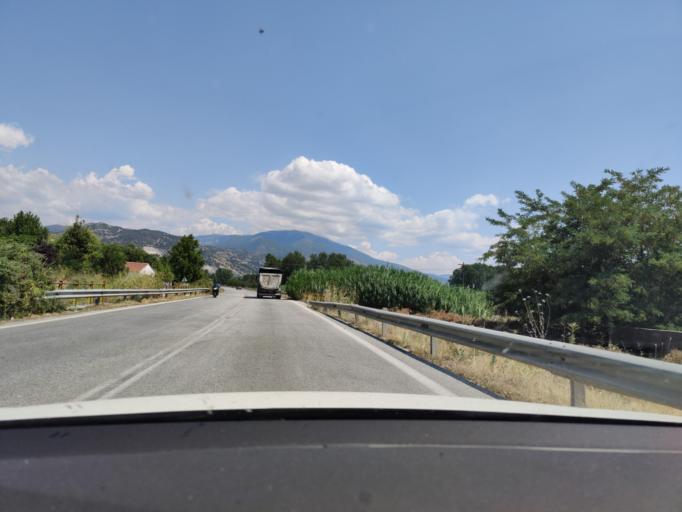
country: GR
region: Central Macedonia
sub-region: Nomos Serron
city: Serres
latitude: 41.0784
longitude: 23.5694
